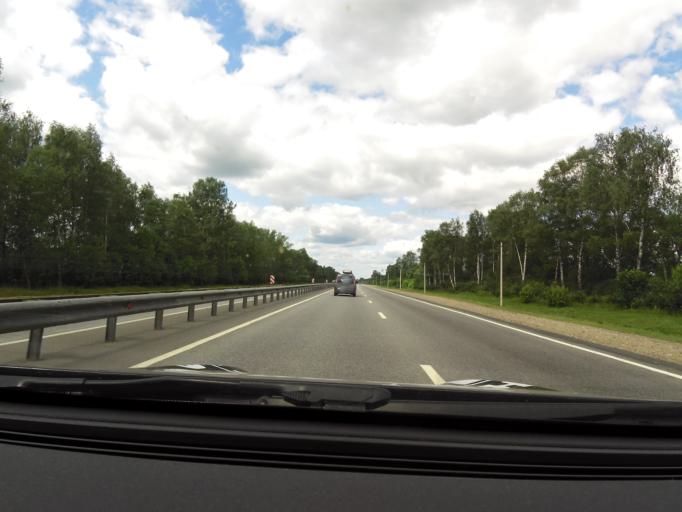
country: RU
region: Tverskaya
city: Torzhok
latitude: 57.0057
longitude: 35.1248
